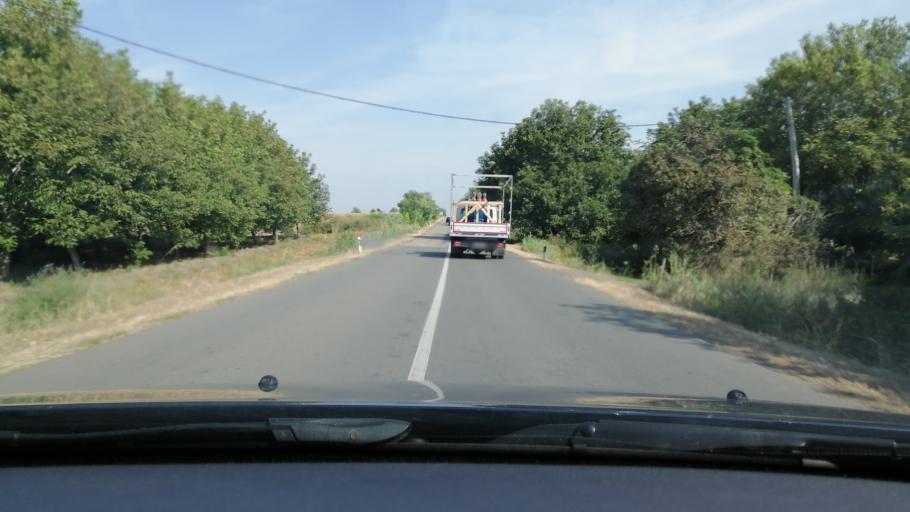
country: RS
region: Autonomna Pokrajina Vojvodina
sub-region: Juznobanatski Okrug
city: Kovacica
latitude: 45.1209
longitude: 20.6168
